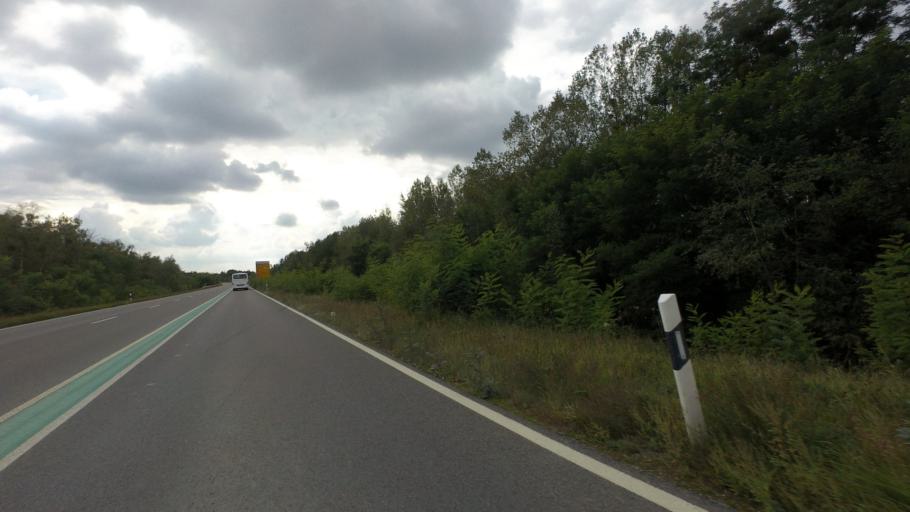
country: DE
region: Brandenburg
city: Senftenberg
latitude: 51.5362
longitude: 14.0268
